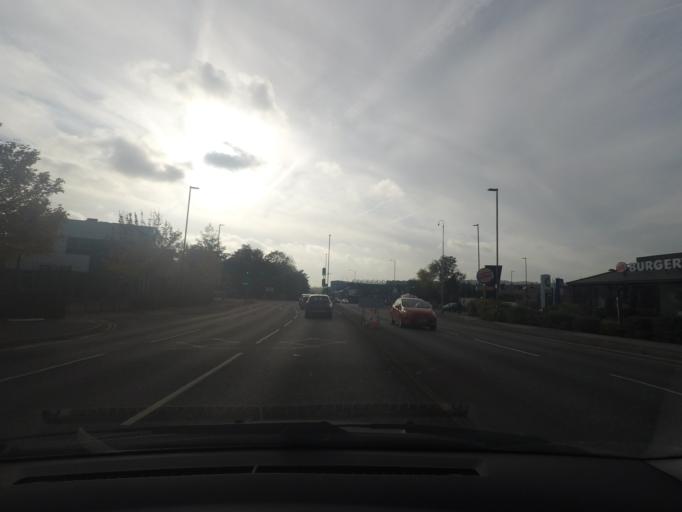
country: GB
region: England
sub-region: Sheffield
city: Oughtibridge
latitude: 53.4156
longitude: -1.5009
